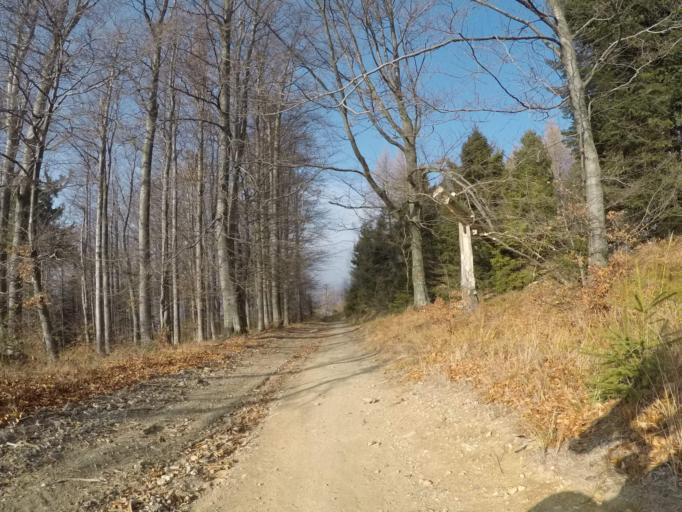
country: SK
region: Kosicky
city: Gelnica
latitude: 48.7593
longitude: 21.0429
